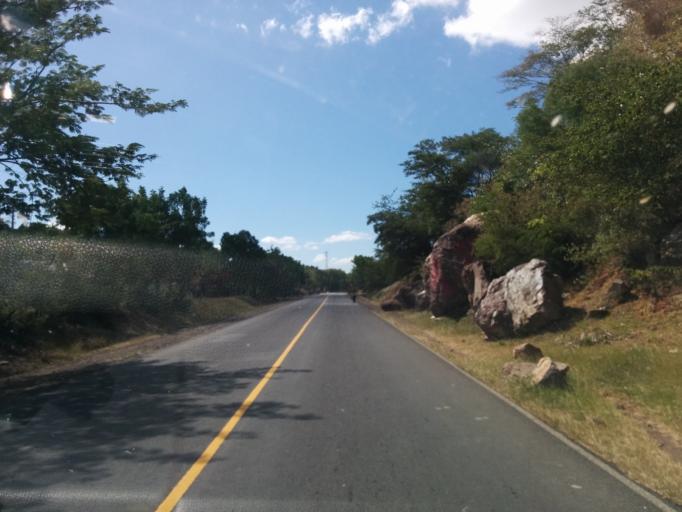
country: NI
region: Matagalpa
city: Ciudad Dario
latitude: 12.8396
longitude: -86.2159
